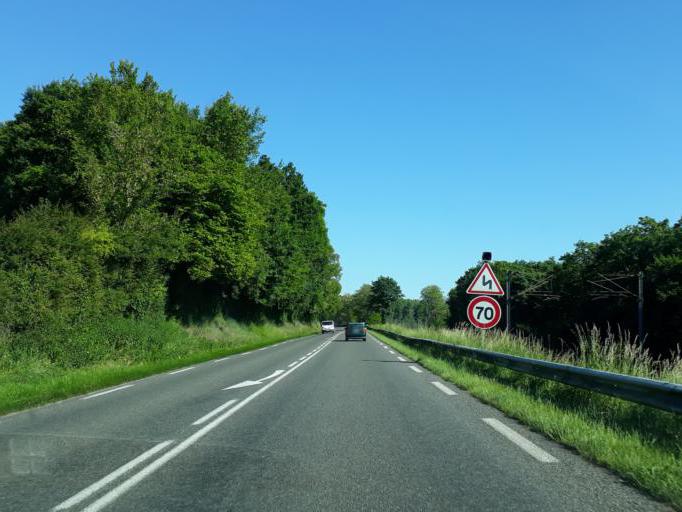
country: FR
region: Bourgogne
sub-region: Departement de la Nievre
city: Neuvy-sur-Loire
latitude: 47.4948
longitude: 2.9134
